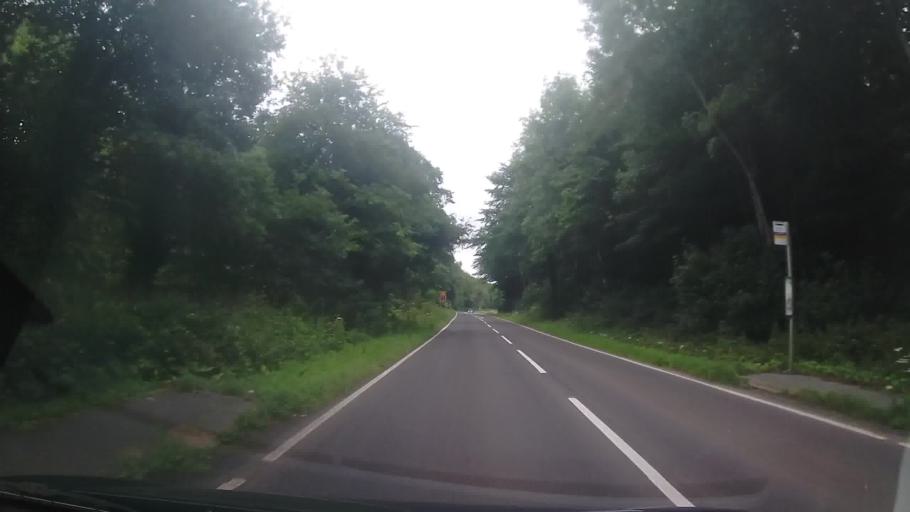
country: GB
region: Wales
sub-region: Gwynedd
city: Y Felinheli
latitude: 53.2045
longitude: -4.2215
